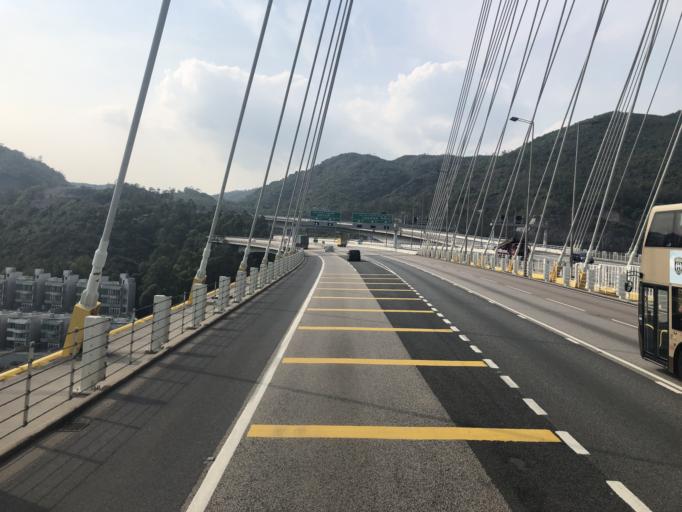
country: HK
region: Tsuen Wan
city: Tsuen Wan
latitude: 22.3675
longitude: 114.0777
